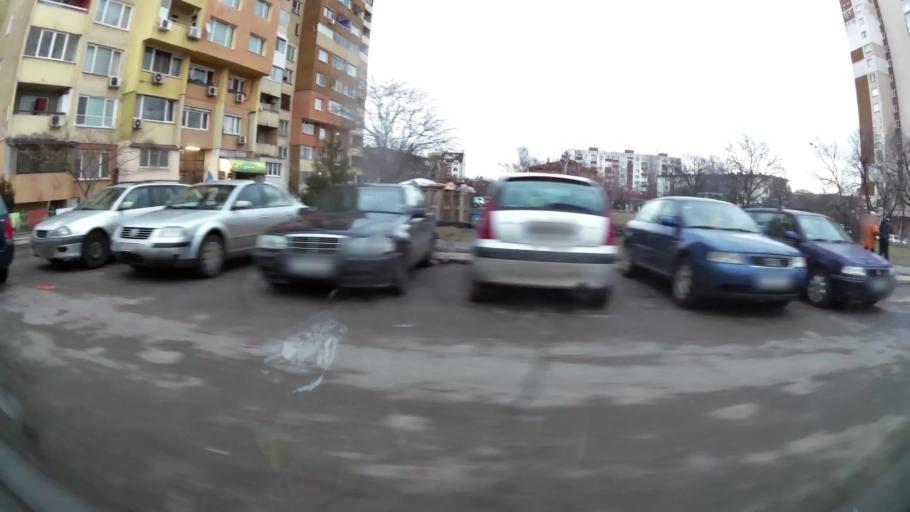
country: BG
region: Sofia-Capital
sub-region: Stolichna Obshtina
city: Sofia
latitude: 42.7352
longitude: 23.2972
